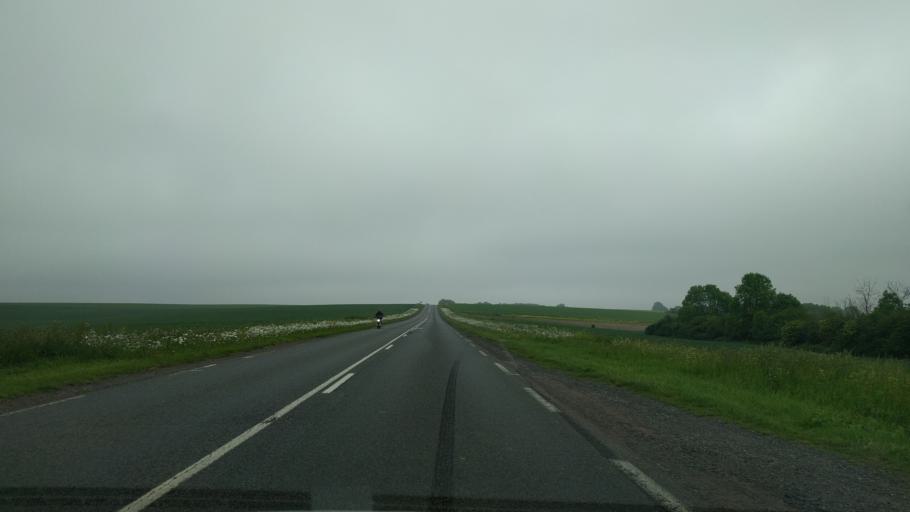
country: FR
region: Picardie
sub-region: Departement de la Somme
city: Peronne
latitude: 49.9659
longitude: 2.9225
